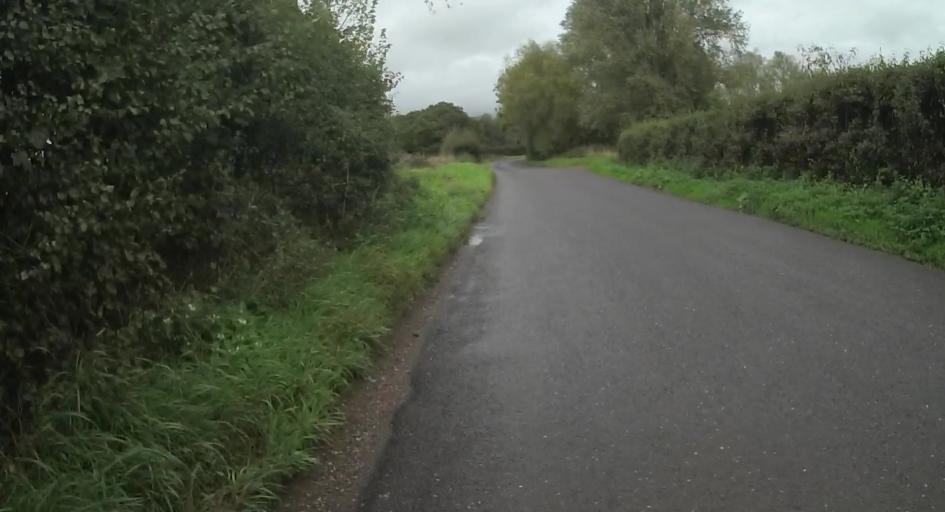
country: GB
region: England
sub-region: Hampshire
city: Tadley
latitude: 51.3039
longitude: -1.1534
